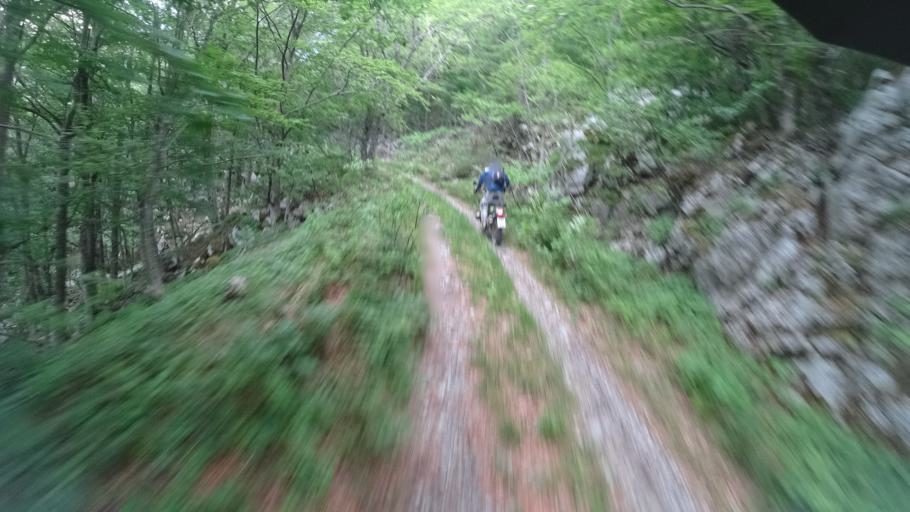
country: HR
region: Licko-Senjska
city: Gospic
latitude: 44.4319
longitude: 15.2879
